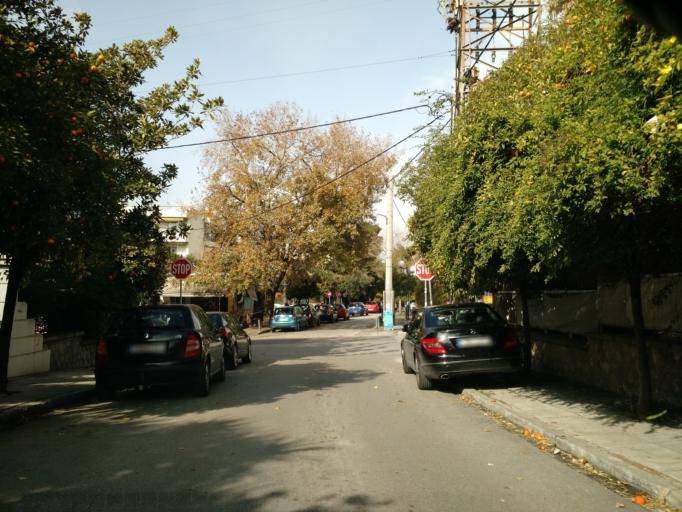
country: GR
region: Attica
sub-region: Nomarchia Athinas
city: Papagou
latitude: 37.9894
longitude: 23.7942
